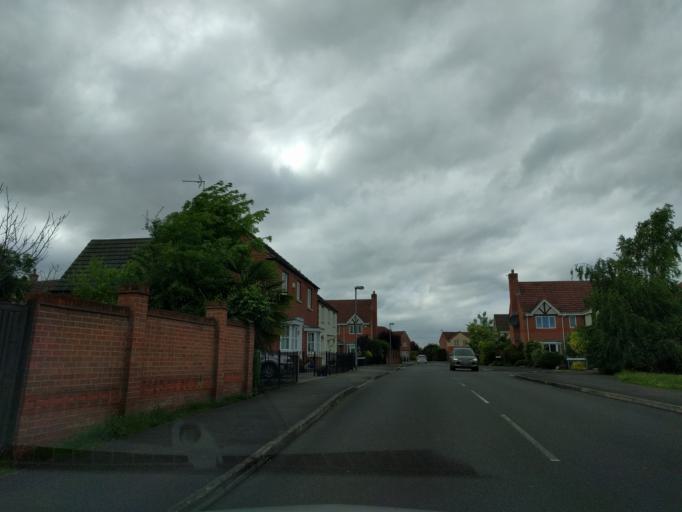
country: GB
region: England
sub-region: Nottinghamshire
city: Newark on Trent
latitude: 53.0778
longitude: -0.7794
